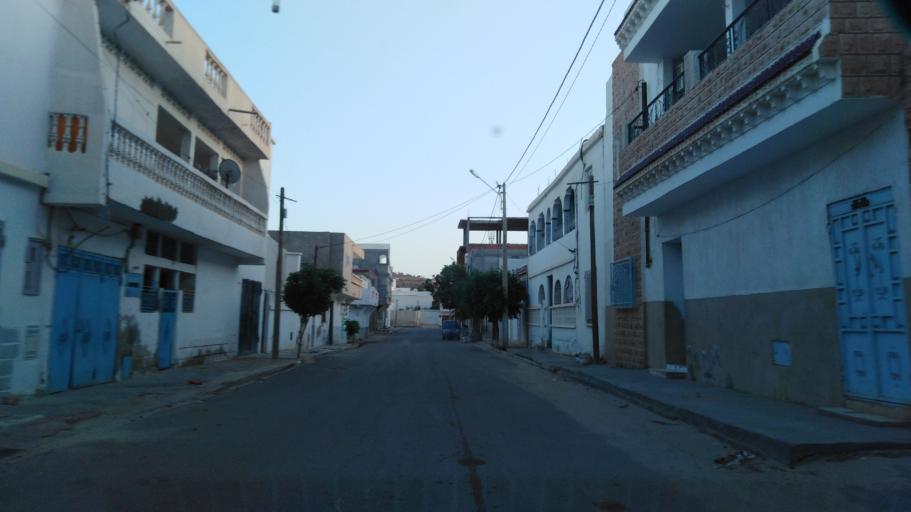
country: TN
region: Tataouine
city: Tataouine
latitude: 32.9352
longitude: 10.4537
